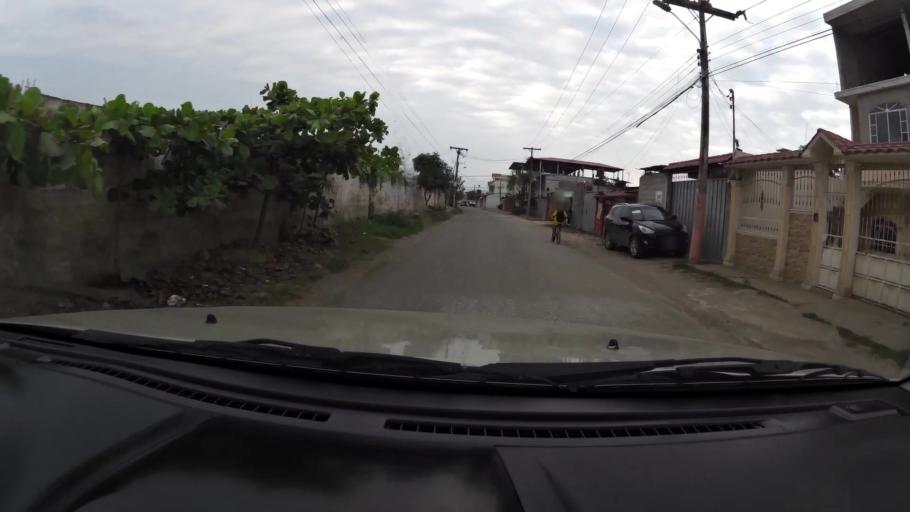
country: EC
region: El Oro
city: Machala
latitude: -3.2681
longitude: -79.9351
